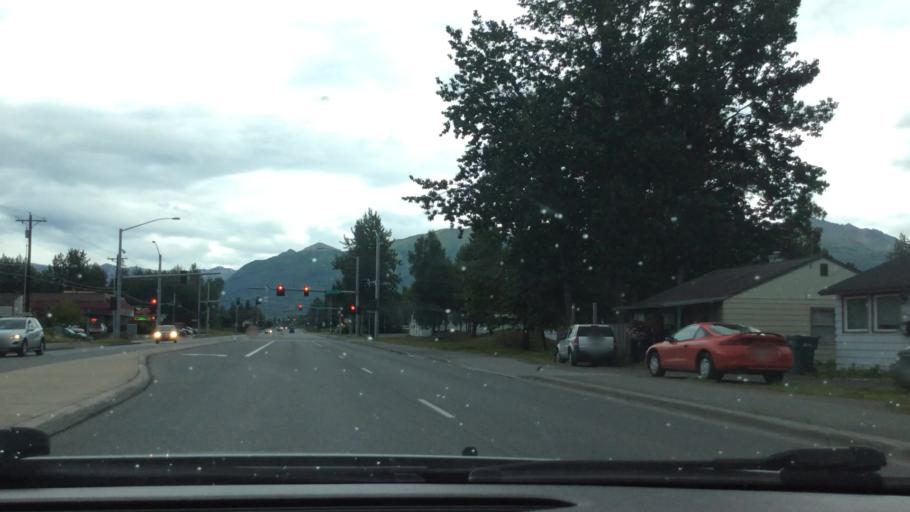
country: US
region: Alaska
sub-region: Anchorage Municipality
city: Anchorage
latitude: 61.2097
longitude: -149.7659
